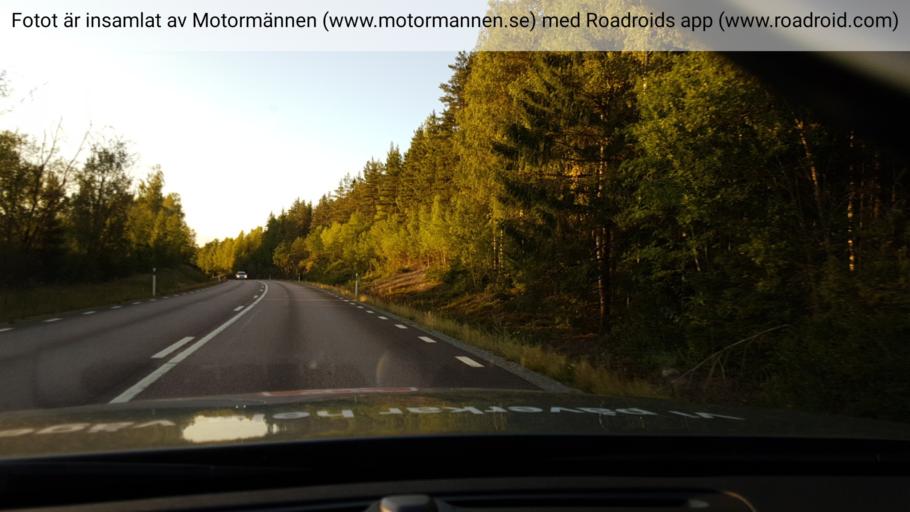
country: SE
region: OErebro
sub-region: Karlskoga Kommun
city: Karlskoga
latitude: 59.4233
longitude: 14.4281
